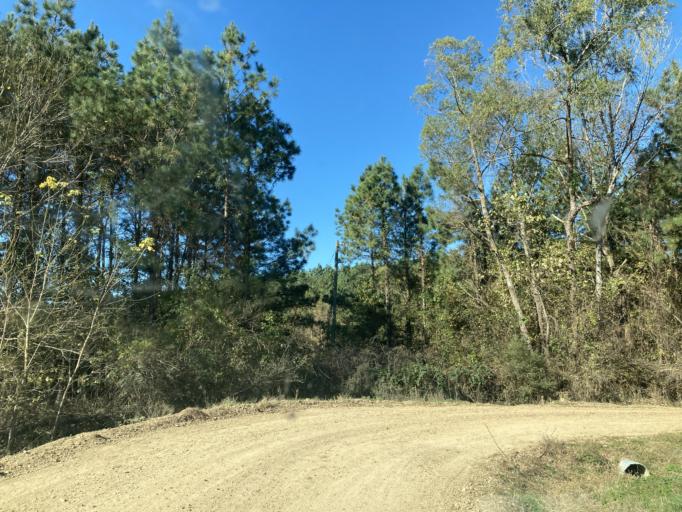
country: US
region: Mississippi
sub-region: Madison County
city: Kearney Park
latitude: 32.6709
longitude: -90.3404
